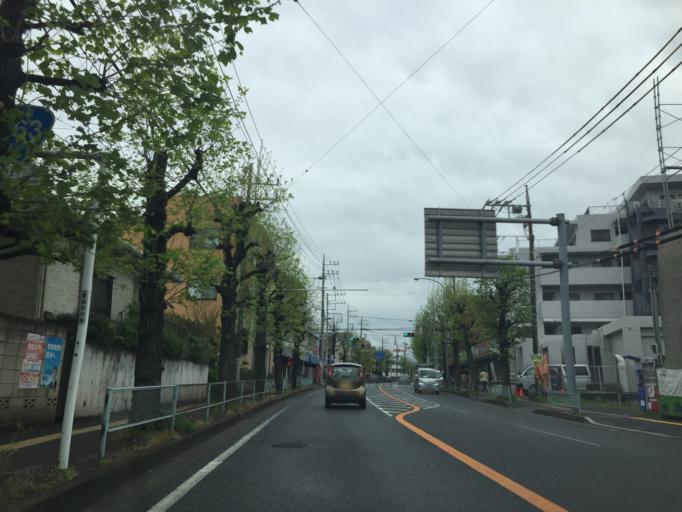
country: JP
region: Saitama
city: Yono
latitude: 35.8702
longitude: 139.6236
